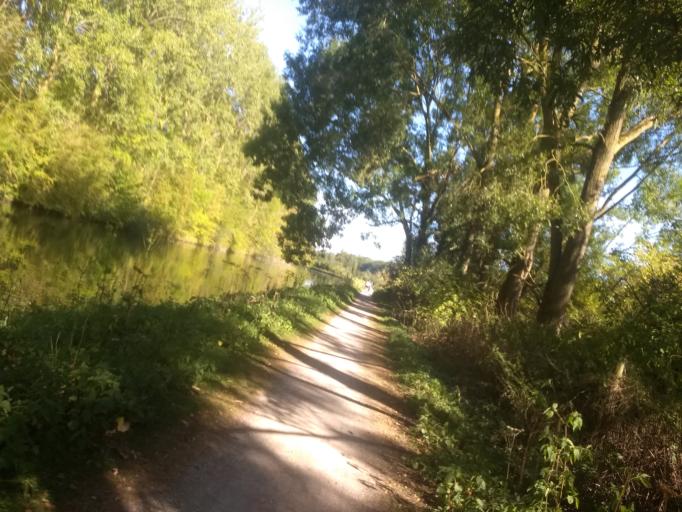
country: FR
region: Nord-Pas-de-Calais
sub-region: Departement du Pas-de-Calais
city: Feuchy
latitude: 50.2960
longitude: 2.8561
